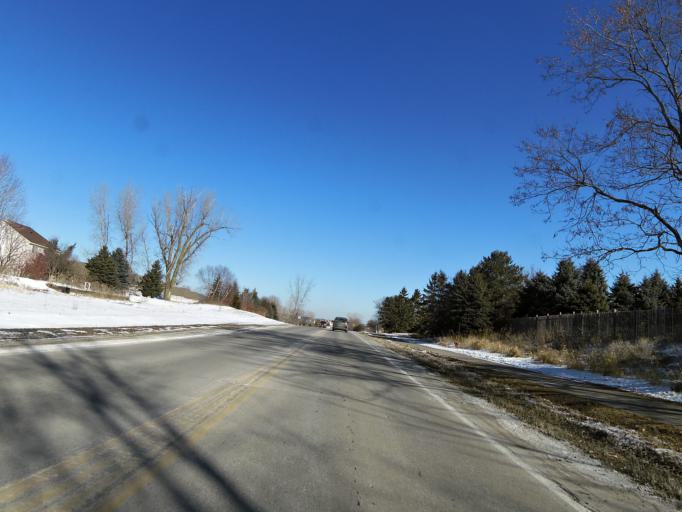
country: US
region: Minnesota
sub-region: Washington County
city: Woodbury
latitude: 44.9081
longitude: -92.9288
